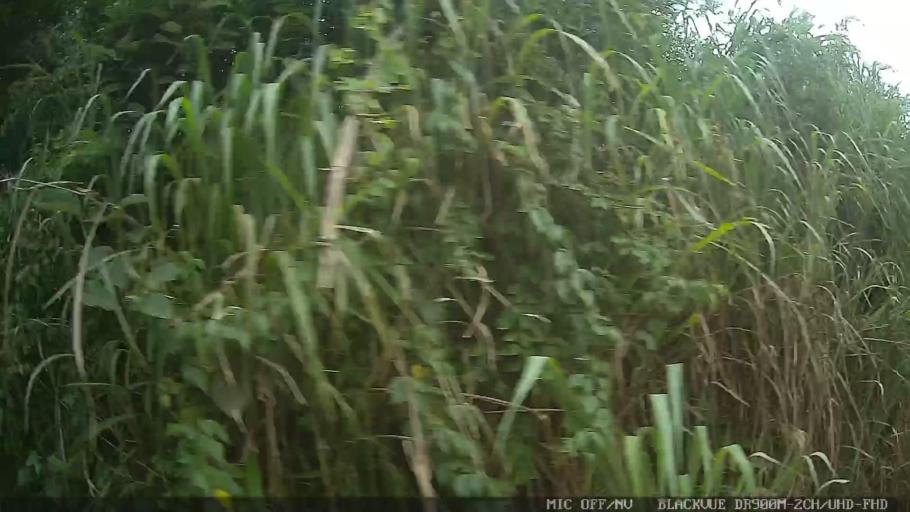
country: BR
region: Sao Paulo
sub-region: Mogi das Cruzes
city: Mogi das Cruzes
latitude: -23.4357
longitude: -46.2287
